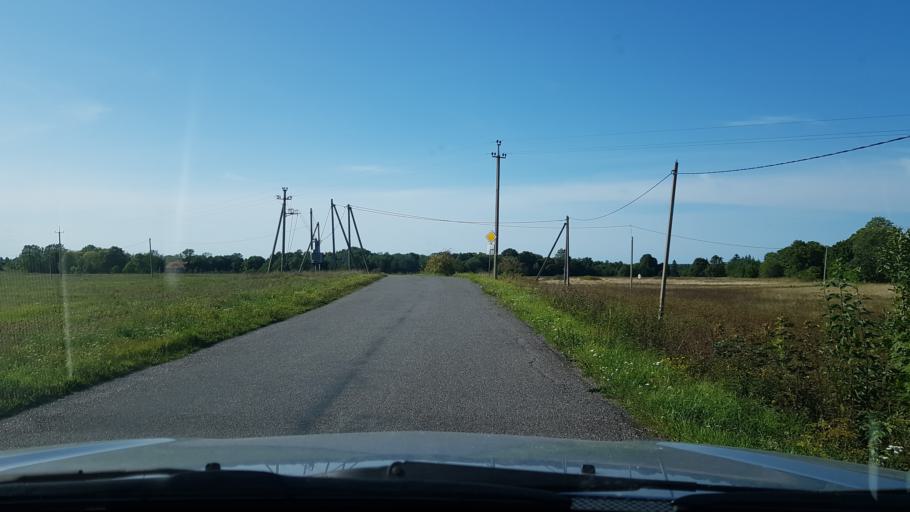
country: EE
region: Ida-Virumaa
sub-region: Narva-Joesuu linn
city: Narva-Joesuu
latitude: 59.4085
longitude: 28.0277
